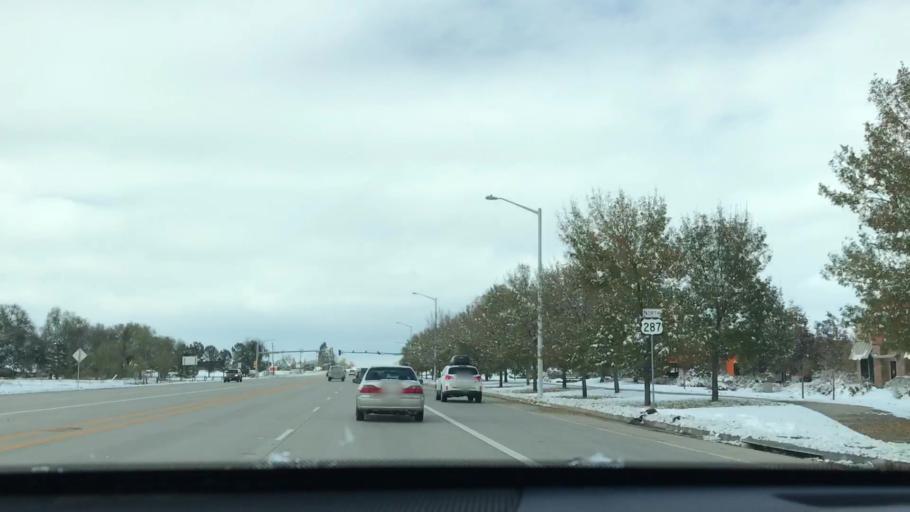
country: US
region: Colorado
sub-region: Boulder County
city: Longmont
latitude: 40.2043
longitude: -105.1021
